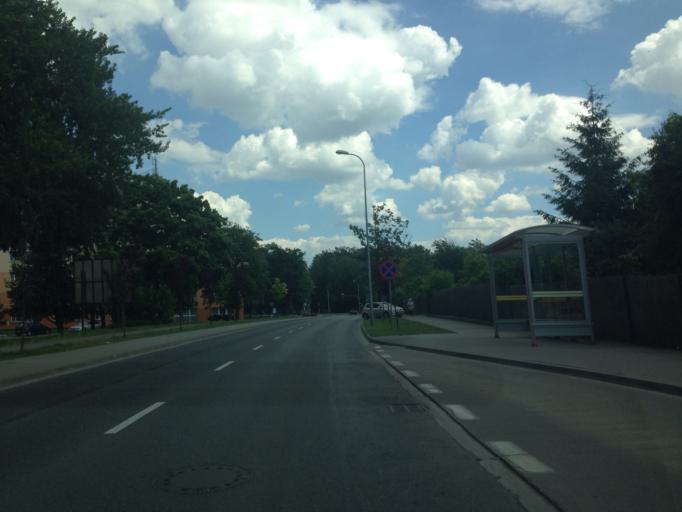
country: PL
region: Masovian Voivodeship
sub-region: Warszawa
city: Bemowo
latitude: 52.2497
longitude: 20.8950
